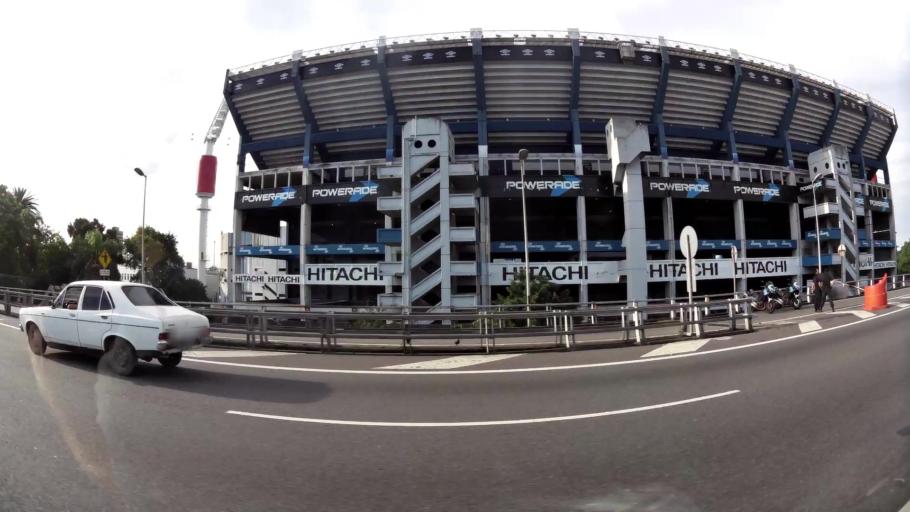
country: AR
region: Buenos Aires F.D.
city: Villa Santa Rita
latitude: -34.6368
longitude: -58.5205
